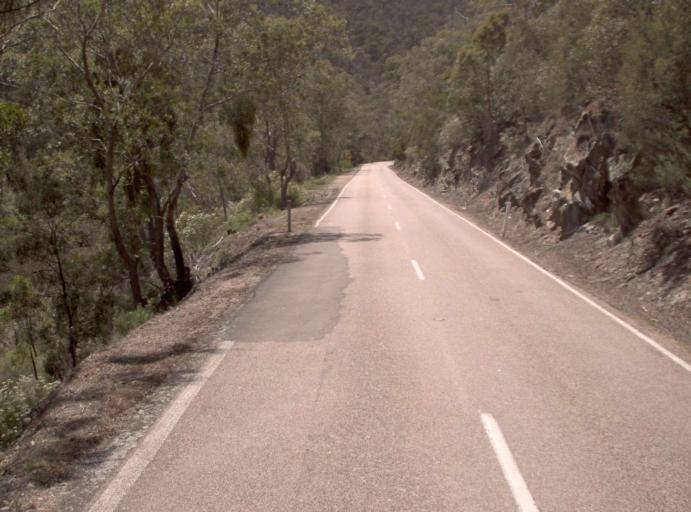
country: AU
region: Victoria
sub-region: East Gippsland
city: Lakes Entrance
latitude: -37.5352
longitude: 147.8588
